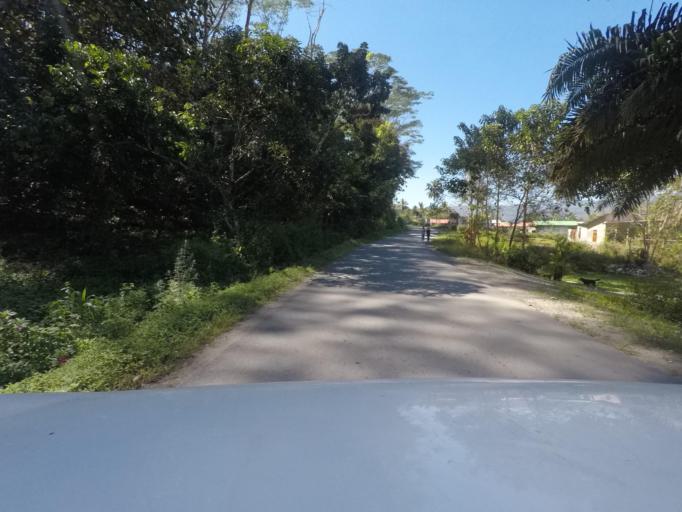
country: TL
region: Ermera
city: Gleno
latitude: -8.7111
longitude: 125.4410
